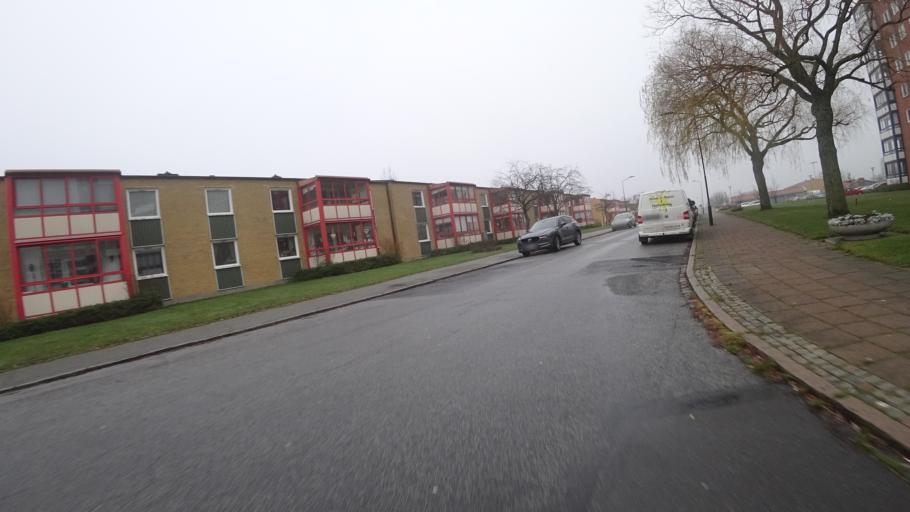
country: SE
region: Skane
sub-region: Malmo
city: Malmoe
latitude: 55.5689
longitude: 13.0050
